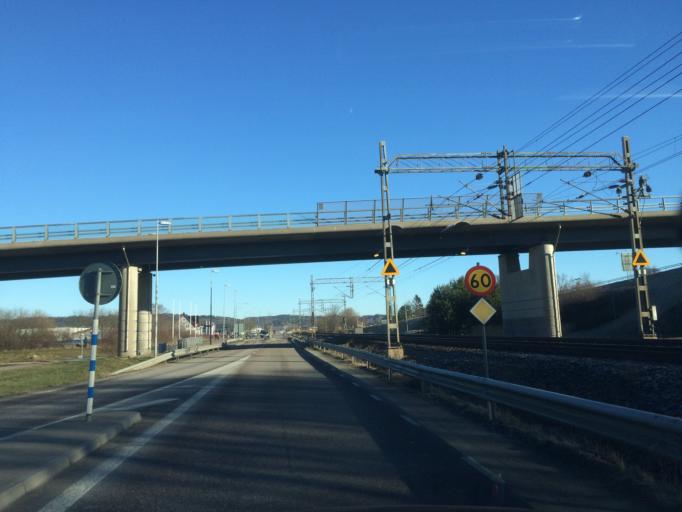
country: SE
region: Halland
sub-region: Kungsbacka Kommun
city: Kungsbacka
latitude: 57.4997
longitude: 12.0802
